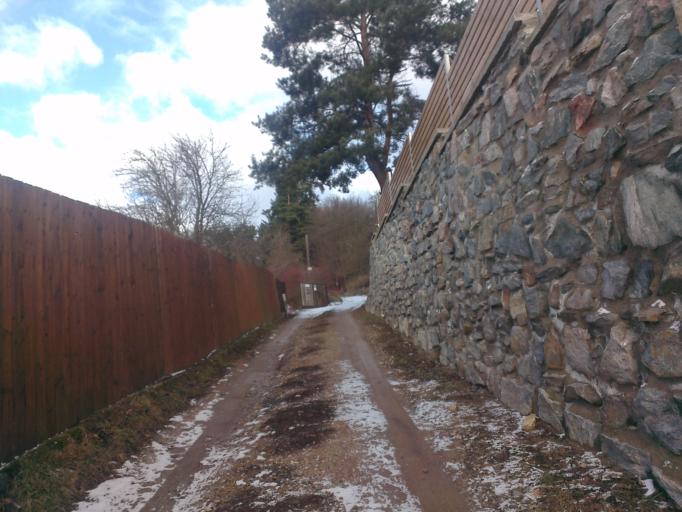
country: CZ
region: South Moravian
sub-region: Okres Brno-Venkov
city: Lelekovice
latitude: 49.2918
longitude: 16.5854
